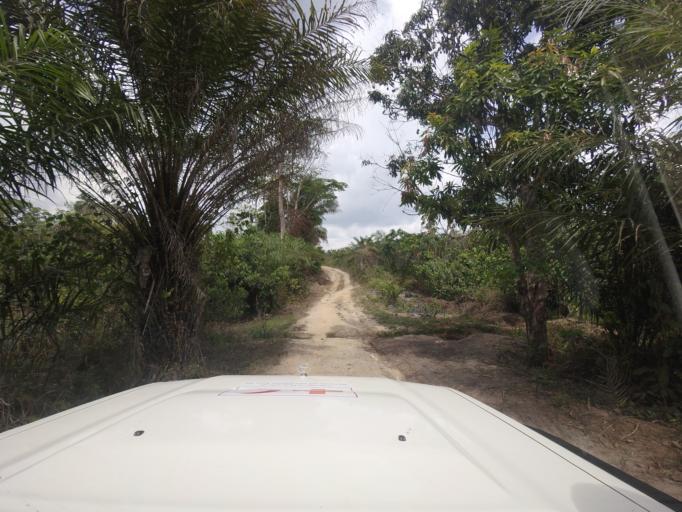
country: LR
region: Lofa
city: Voinjama
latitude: 8.3920
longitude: -9.6113
